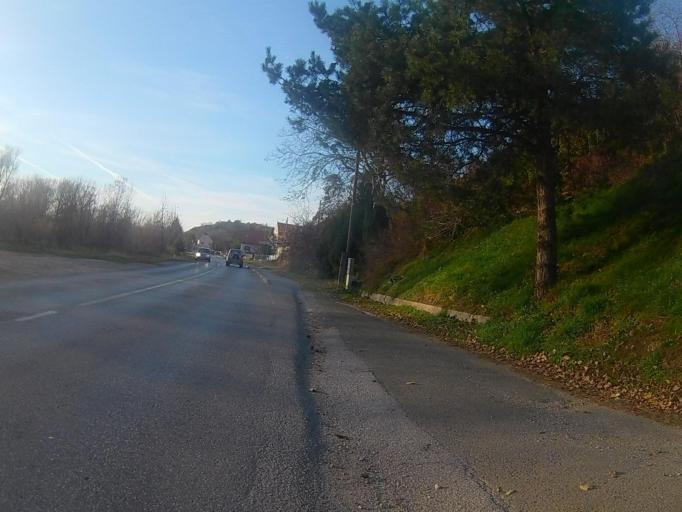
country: SI
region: Duplek
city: Zgornji Duplek
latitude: 46.5545
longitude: 15.6995
